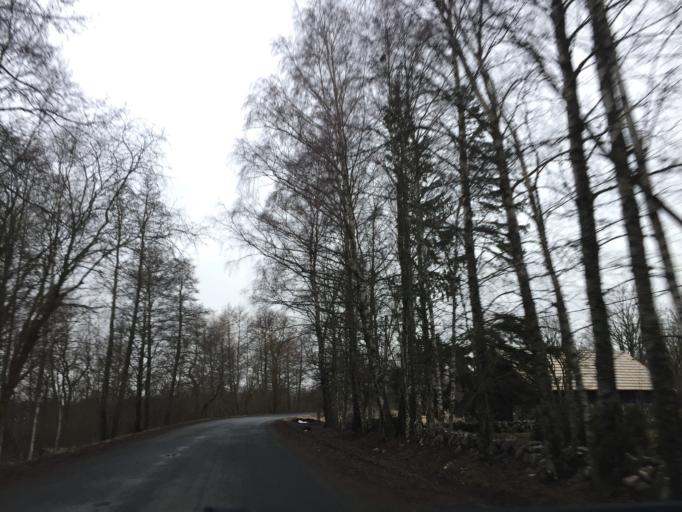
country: EE
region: Laeaene
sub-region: Haapsalu linn
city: Haapsalu
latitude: 58.7817
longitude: 23.4736
